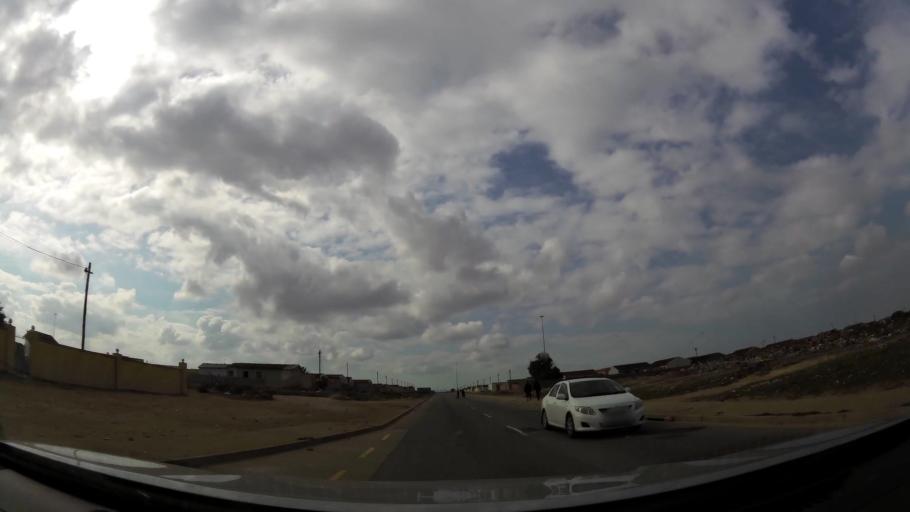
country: ZA
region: Eastern Cape
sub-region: Nelson Mandela Bay Metropolitan Municipality
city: Port Elizabeth
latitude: -33.8216
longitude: 25.5913
